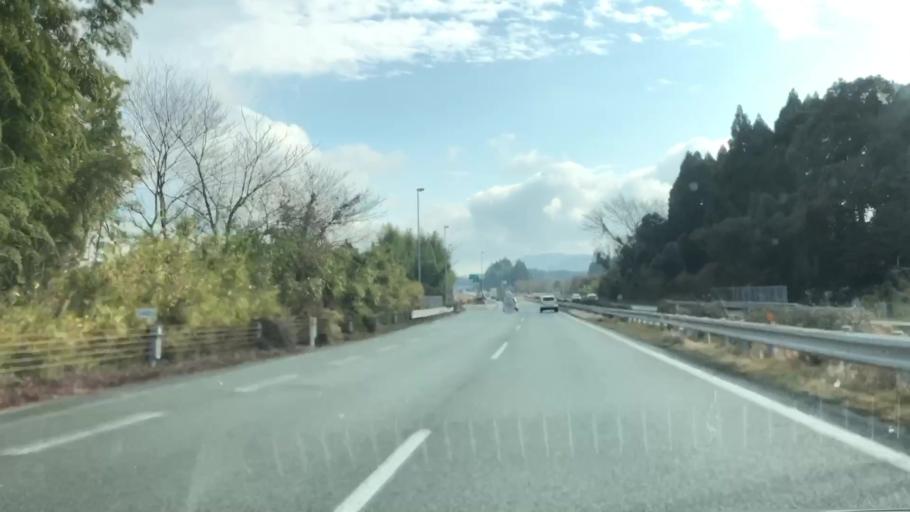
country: JP
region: Kumamoto
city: Tamana
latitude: 32.9897
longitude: 130.6036
